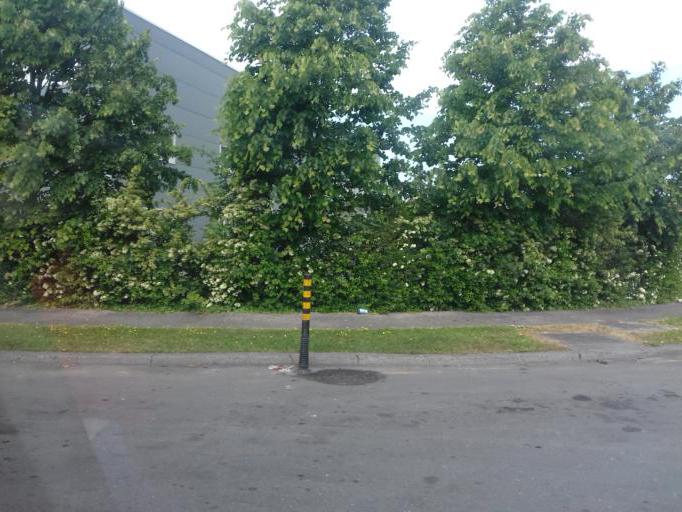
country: IE
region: Leinster
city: Donabate
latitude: 53.4913
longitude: -6.1903
